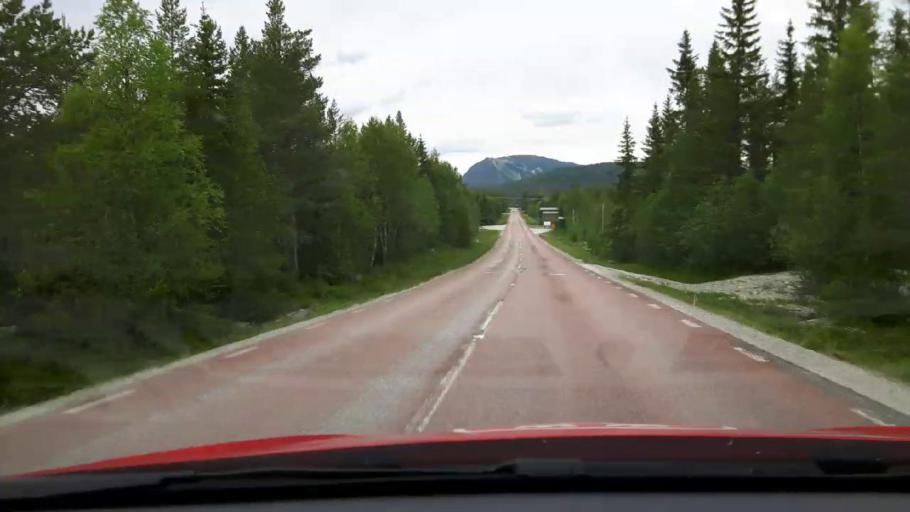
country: NO
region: Hedmark
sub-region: Engerdal
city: Engerdal
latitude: 62.5148
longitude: 12.6032
